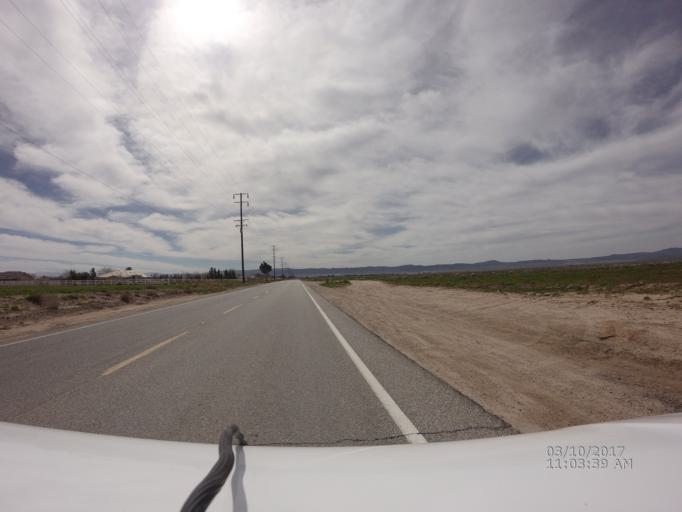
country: US
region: California
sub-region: Los Angeles County
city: Quartz Hill
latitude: 34.7759
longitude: -118.2903
